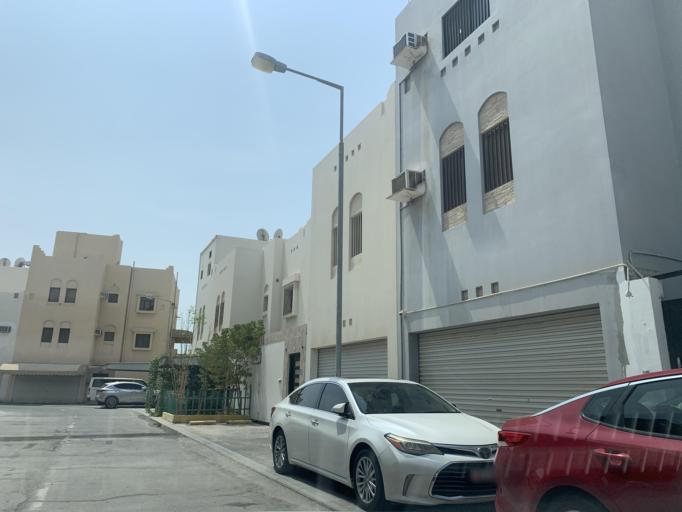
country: BH
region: Muharraq
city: Al Hadd
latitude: 26.2727
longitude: 50.6581
